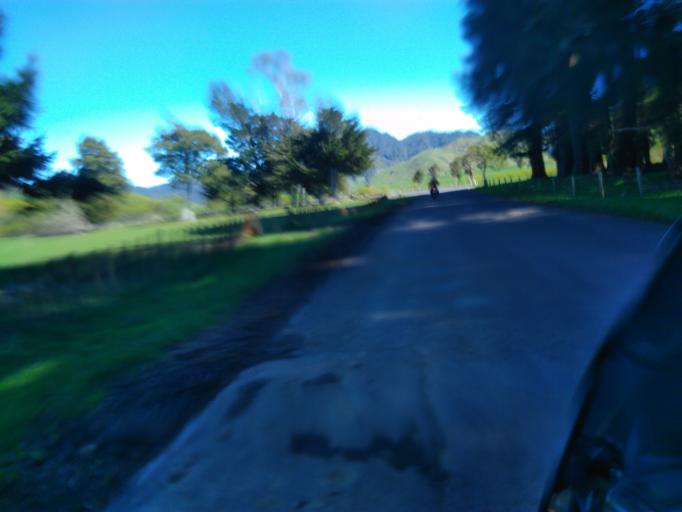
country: NZ
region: Bay of Plenty
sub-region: Opotiki District
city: Opotiki
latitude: -38.2826
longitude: 177.5366
